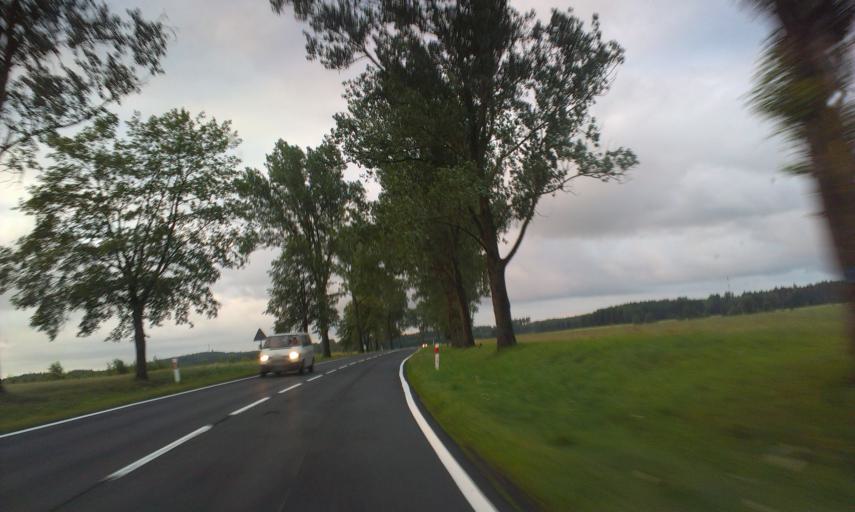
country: PL
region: Greater Poland Voivodeship
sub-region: Powiat zlotowski
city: Okonek
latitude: 53.5636
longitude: 16.8334
